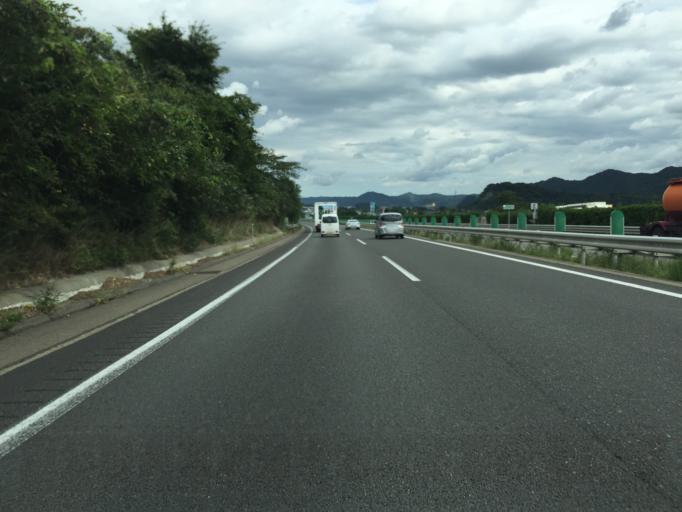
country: JP
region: Miyagi
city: Shiroishi
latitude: 38.0164
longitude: 140.6195
